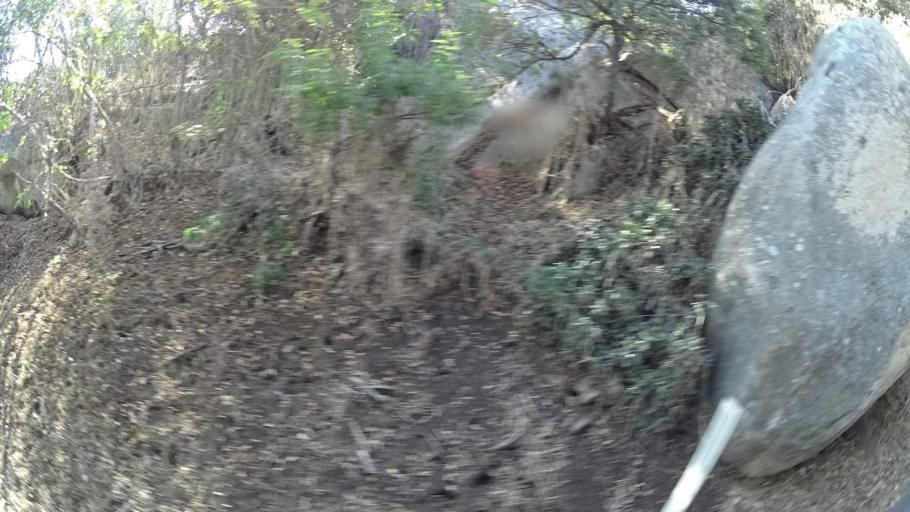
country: US
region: California
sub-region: San Diego County
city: Casa de Oro-Mount Helix
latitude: 32.7750
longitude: -116.9875
